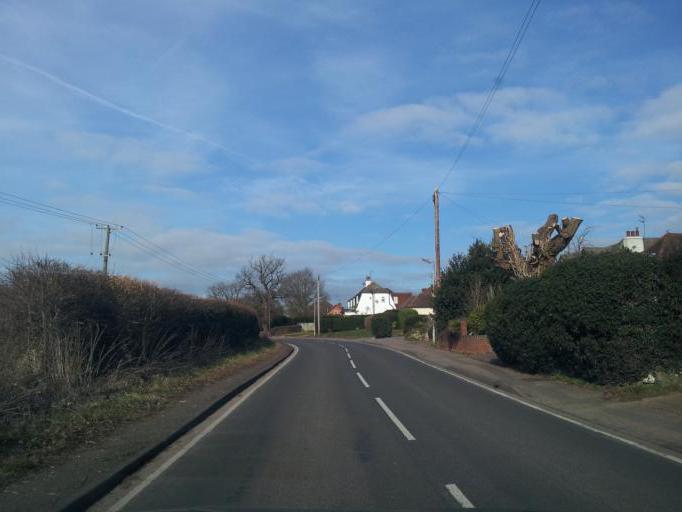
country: GB
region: England
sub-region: Hertfordshire
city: St Albans
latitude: 51.7460
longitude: -0.2798
